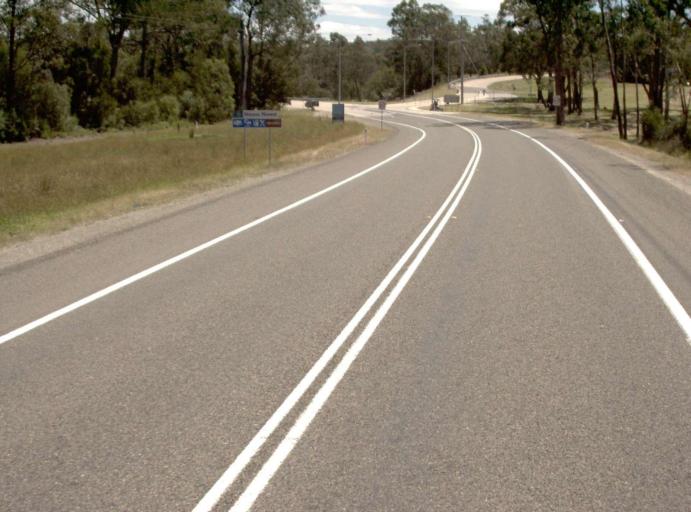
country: AU
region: Victoria
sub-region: East Gippsland
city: Lakes Entrance
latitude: -37.7308
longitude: 148.0975
